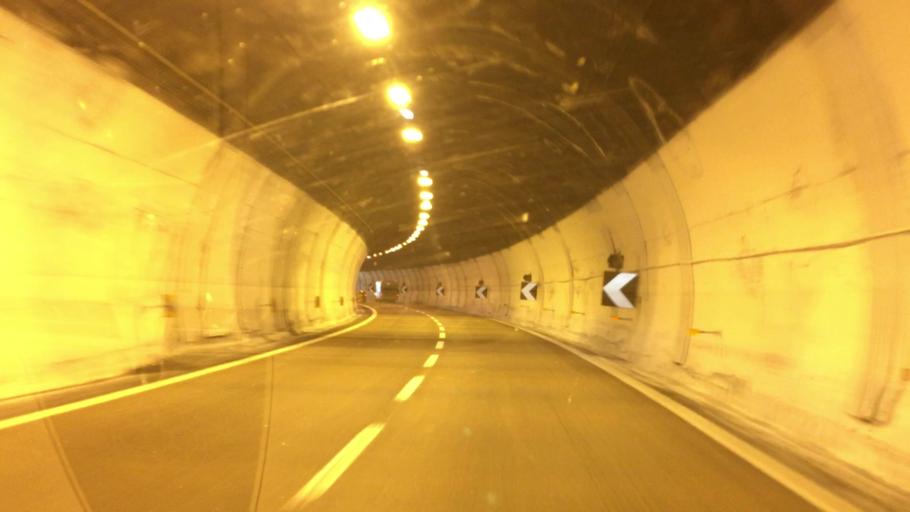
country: IT
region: Liguria
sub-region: Provincia di Genova
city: Sestri Levante
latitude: 44.2853
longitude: 9.3961
